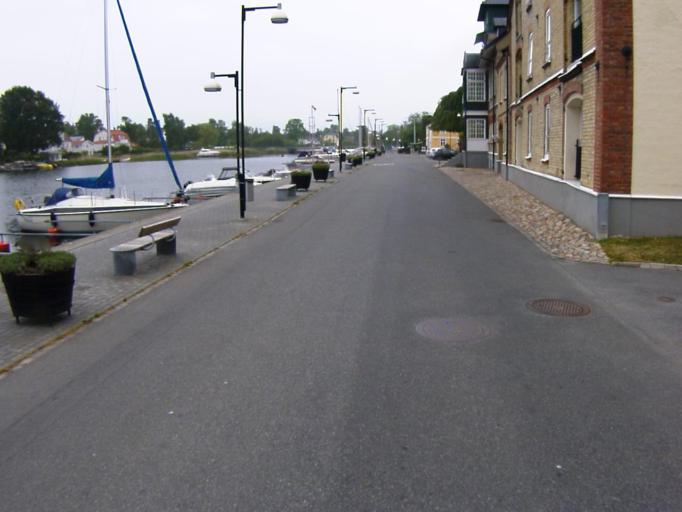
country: SE
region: Skane
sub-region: Kristianstads Kommun
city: Ahus
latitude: 55.9225
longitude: 14.2969
